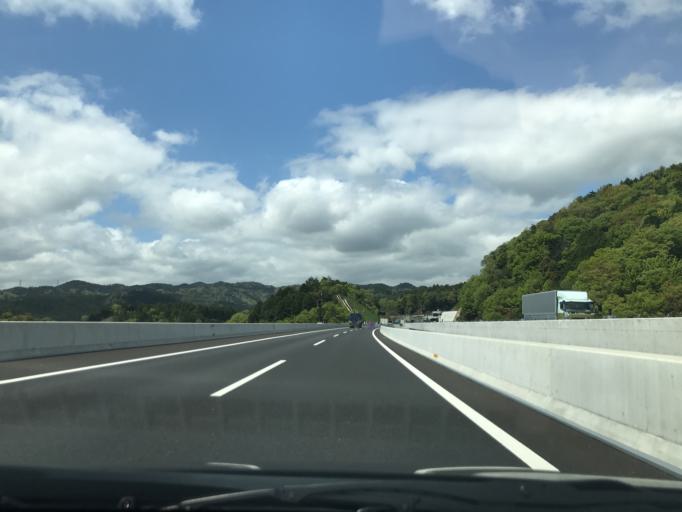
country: JP
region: Osaka
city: Takatsuki
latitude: 34.8896
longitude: 135.6115
